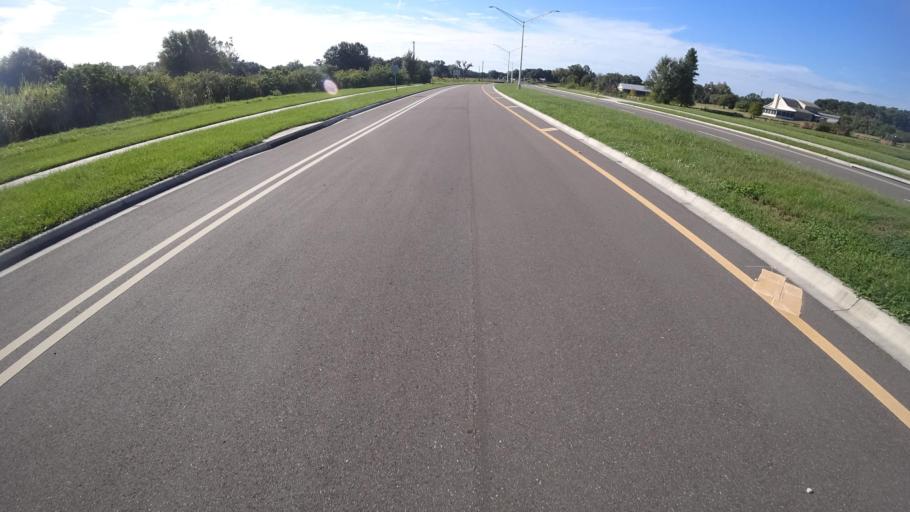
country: US
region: Florida
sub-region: Manatee County
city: Ellenton
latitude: 27.5786
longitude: -82.4352
